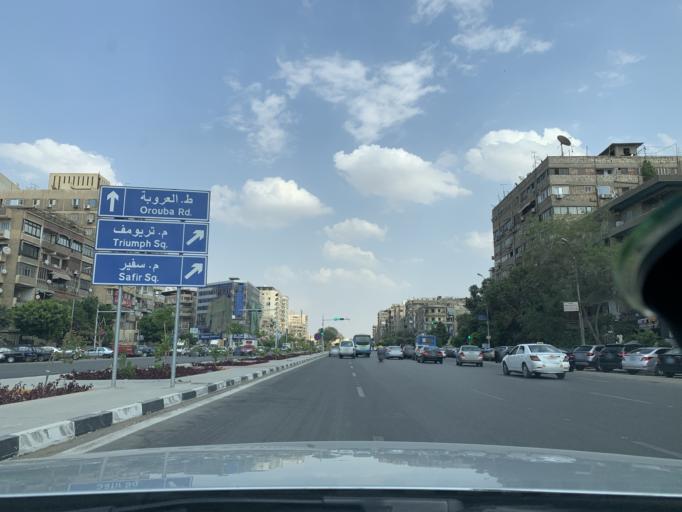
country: EG
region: Muhafazat al Qahirah
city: Cairo
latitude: 30.1061
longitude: 31.3423
